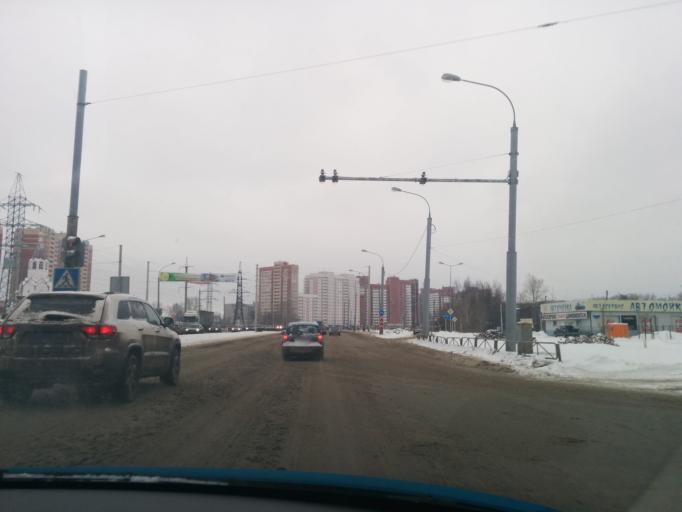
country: RU
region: Perm
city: Perm
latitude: 57.9903
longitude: 56.2970
